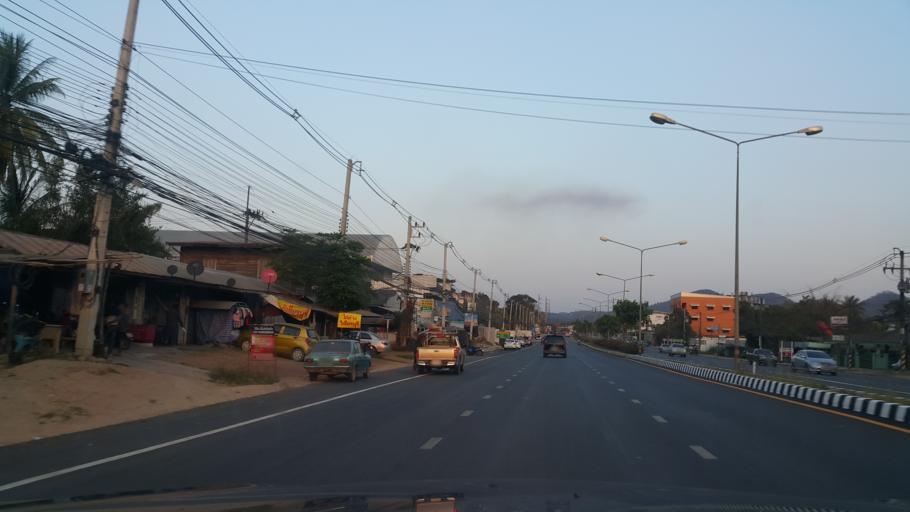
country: TH
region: Loei
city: Loei
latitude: 17.4949
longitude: 101.7162
